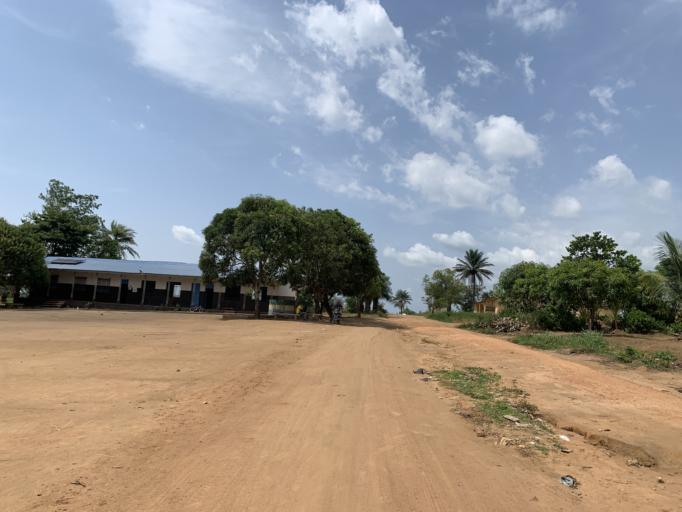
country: SL
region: Western Area
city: Waterloo
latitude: 8.3619
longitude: -13.0441
